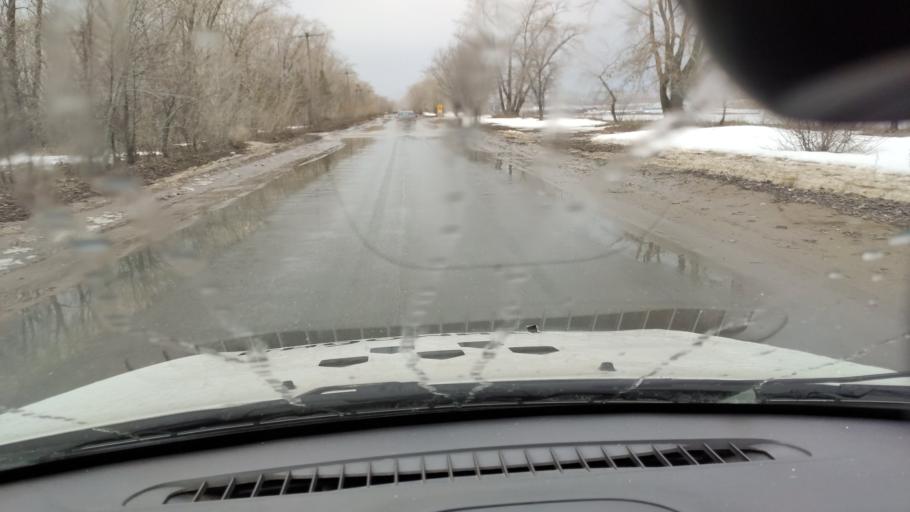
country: RU
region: Samara
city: Zhigulevsk
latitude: 53.4585
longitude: 49.5332
